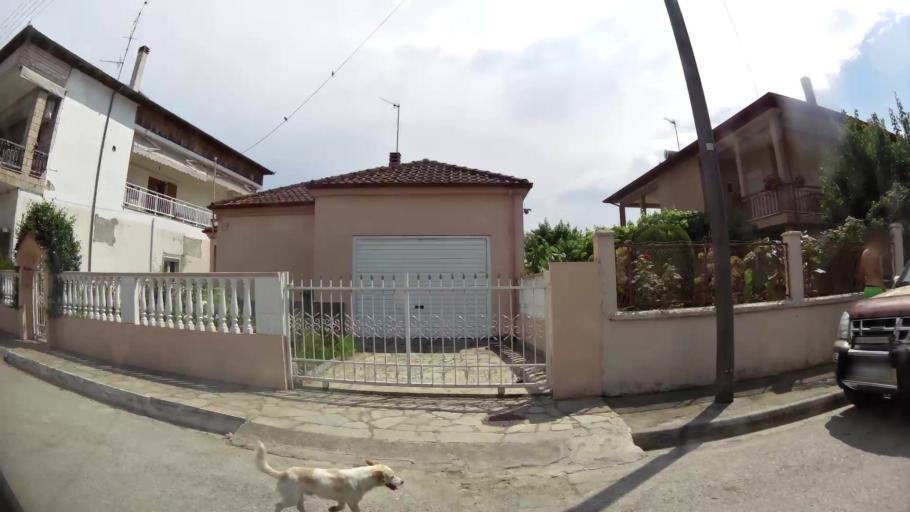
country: GR
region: Central Macedonia
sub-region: Nomos Pierias
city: Korinos
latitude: 40.3199
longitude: 22.5847
